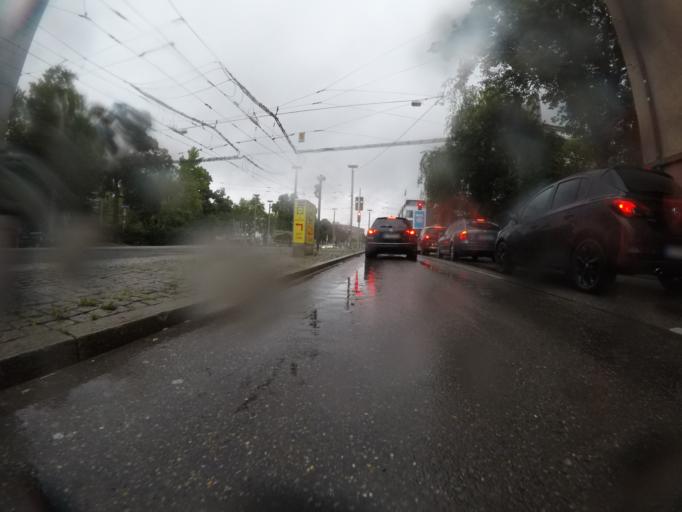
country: DE
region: Baden-Wuerttemberg
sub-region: Regierungsbezirk Stuttgart
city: Stuttgart
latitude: 48.7768
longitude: 9.1668
